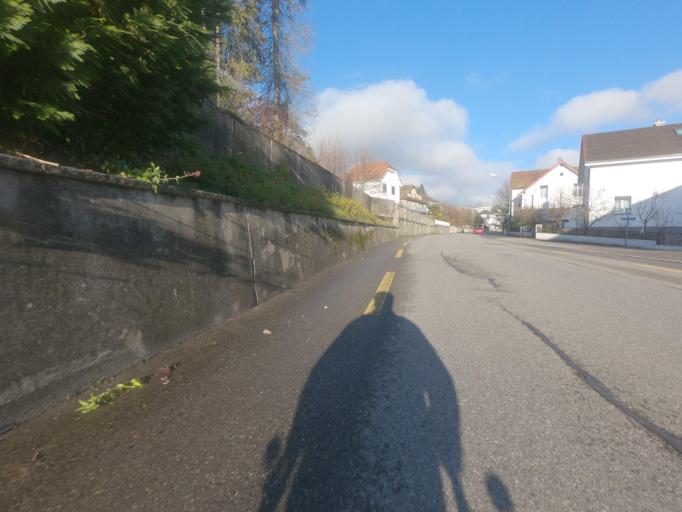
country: CH
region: Solothurn
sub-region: Bezirk Lebern
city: Grenchen
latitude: 47.1951
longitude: 7.4023
